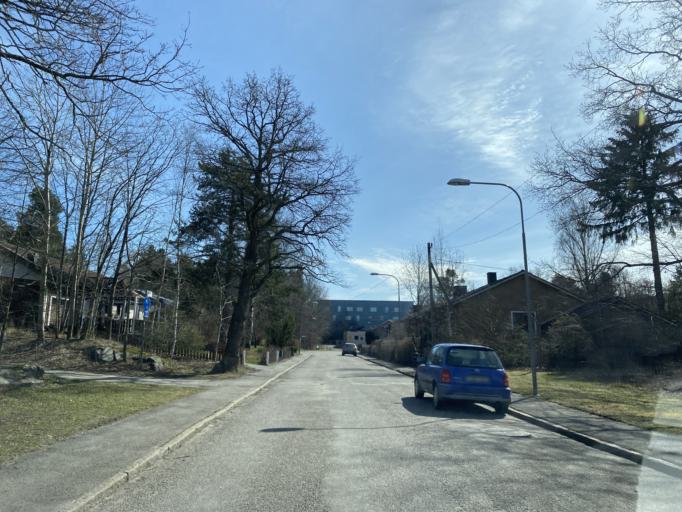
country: SE
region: Stockholm
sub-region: Stockholms Kommun
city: Arsta
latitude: 59.2878
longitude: 18.0131
